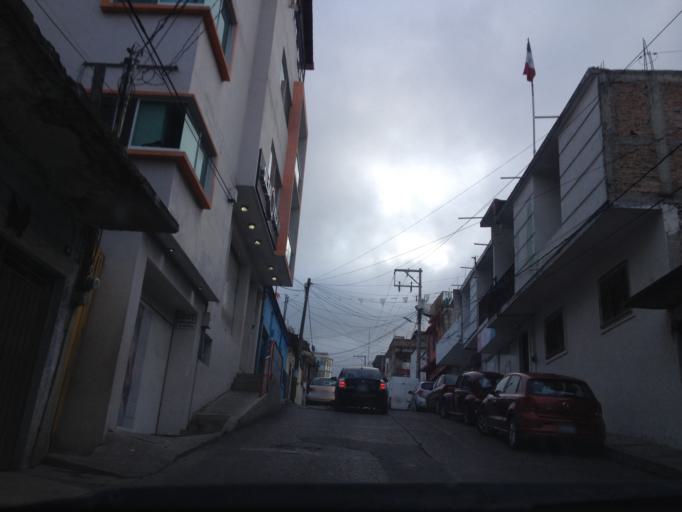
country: MX
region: Guerrero
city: Chilpancingo de los Bravos
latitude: 17.5502
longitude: -99.5036
